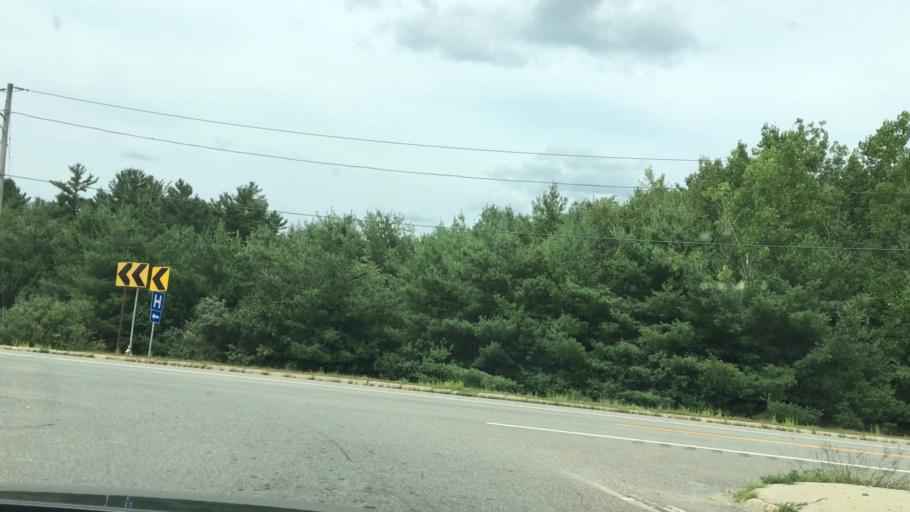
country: US
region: Massachusetts
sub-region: Worcester County
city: Gardner
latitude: 42.6042
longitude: -71.9892
